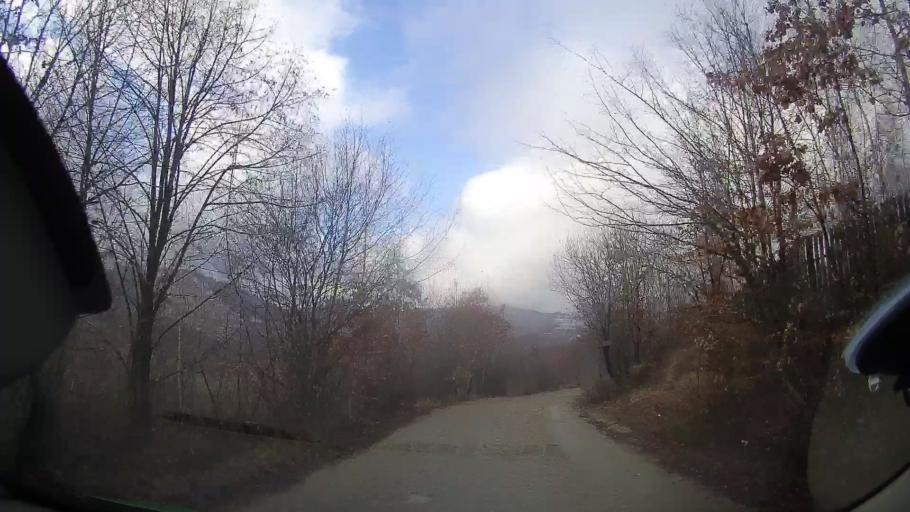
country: RO
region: Cluj
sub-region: Comuna Valea Ierii
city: Valea Ierii
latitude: 46.6784
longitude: 23.3134
